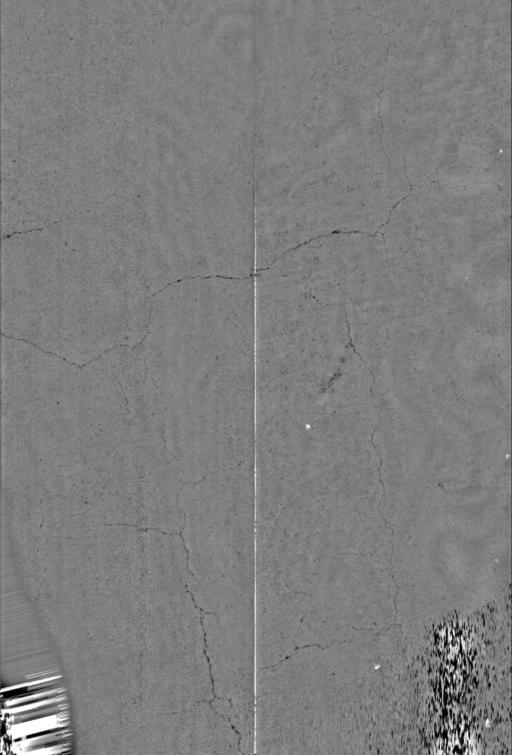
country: US
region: Maryland
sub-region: Prince George's County
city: Silver Hill
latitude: 38.8562
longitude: -76.9568
